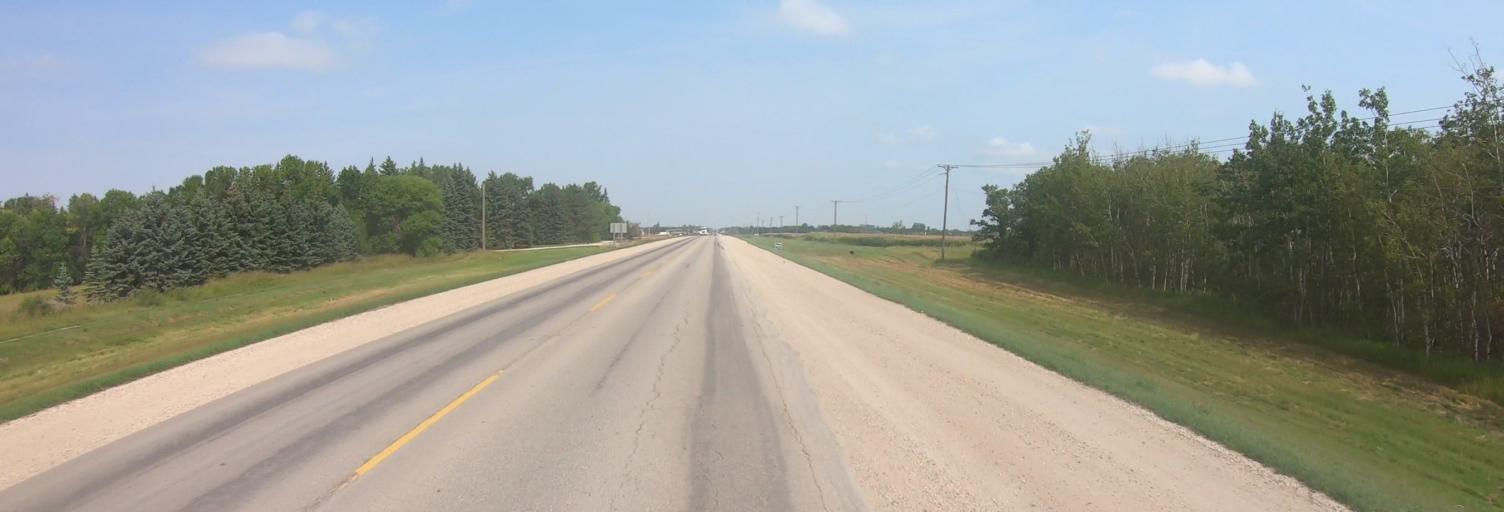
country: CA
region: Manitoba
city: Steinbach
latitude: 49.4981
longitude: -96.6912
